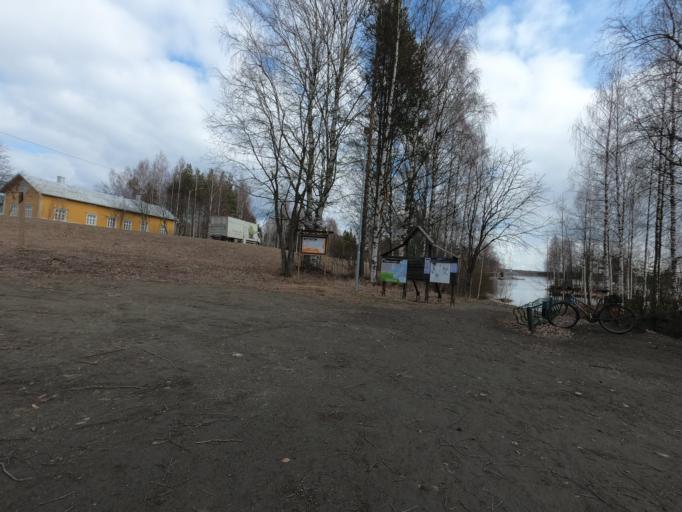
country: FI
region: North Karelia
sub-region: Joensuu
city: Joensuu
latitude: 62.6197
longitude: 29.8678
